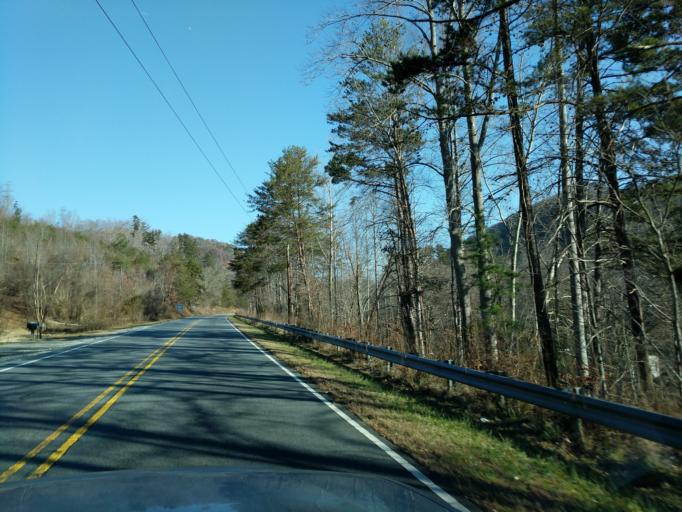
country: US
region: North Carolina
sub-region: McDowell County
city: West Marion
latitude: 35.5231
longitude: -81.9737
